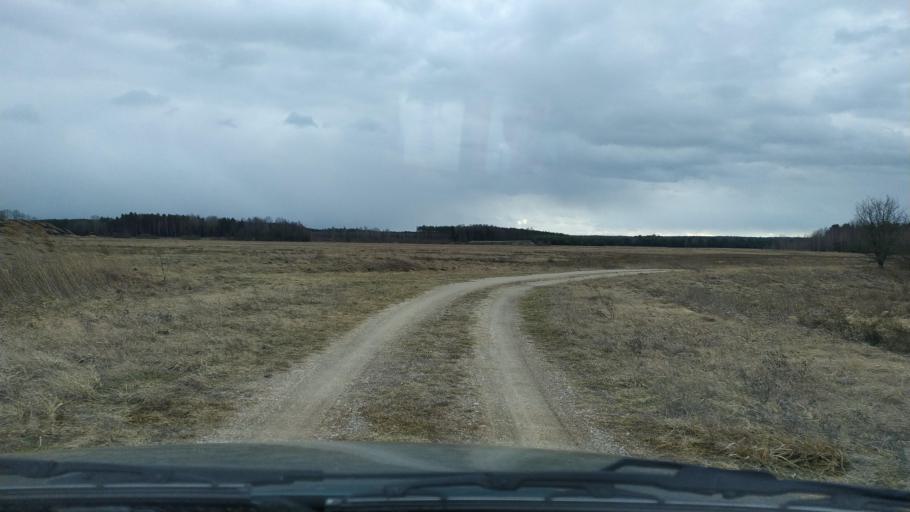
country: BY
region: Brest
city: Zhabinka
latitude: 52.4112
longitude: 24.0692
